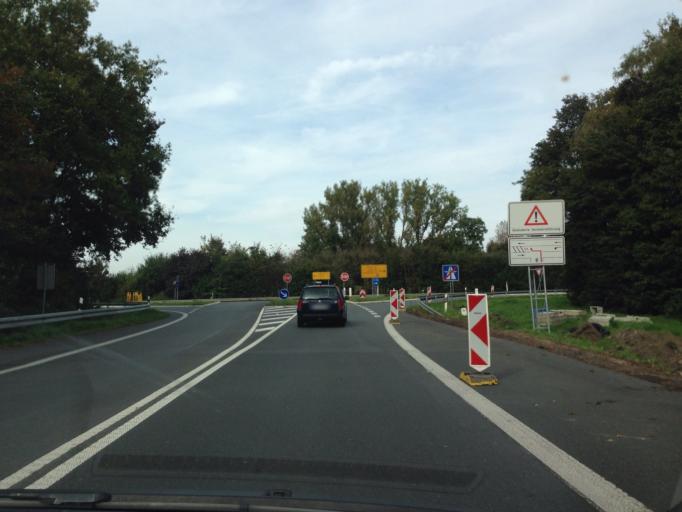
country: DE
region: North Rhine-Westphalia
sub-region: Regierungsbezirk Munster
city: Ascheberg
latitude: 51.7952
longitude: 7.6334
